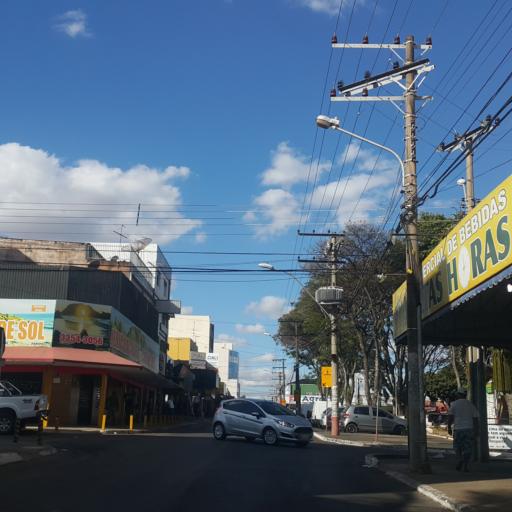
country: BR
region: Federal District
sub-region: Brasilia
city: Brasilia
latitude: -15.8262
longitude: -48.0587
